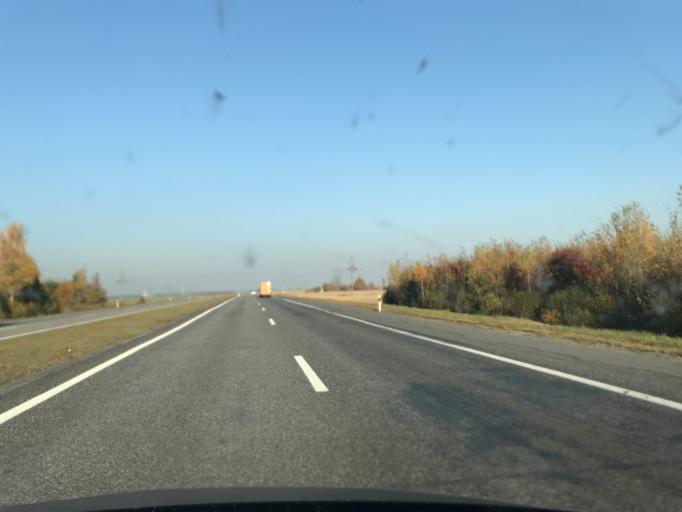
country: BY
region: Minsk
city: Haradzyeya
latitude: 53.3873
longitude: 26.5202
